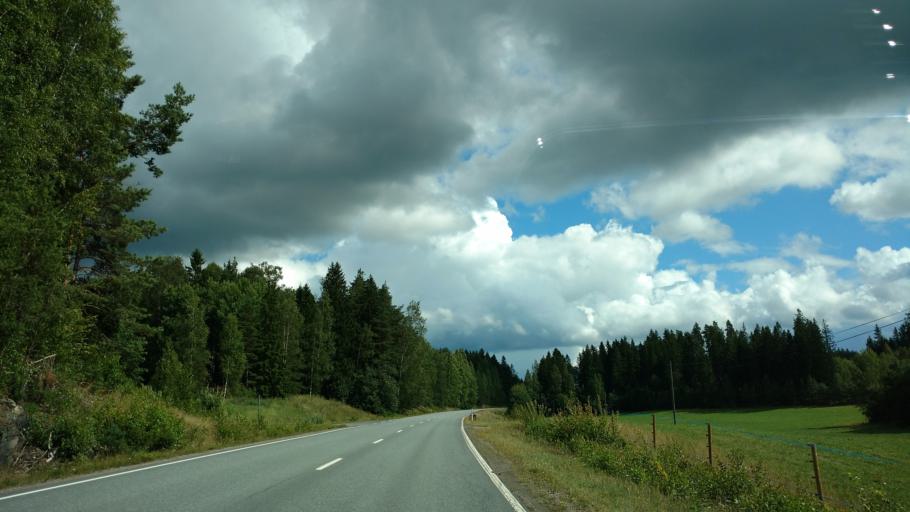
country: FI
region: Varsinais-Suomi
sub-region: Salo
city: Kisko
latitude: 60.2468
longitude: 23.5125
